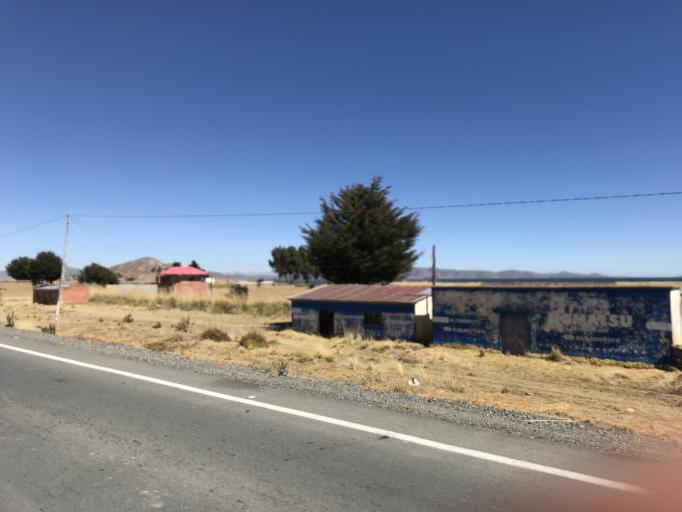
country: BO
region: La Paz
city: Huarina
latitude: -16.2056
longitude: -68.5952
